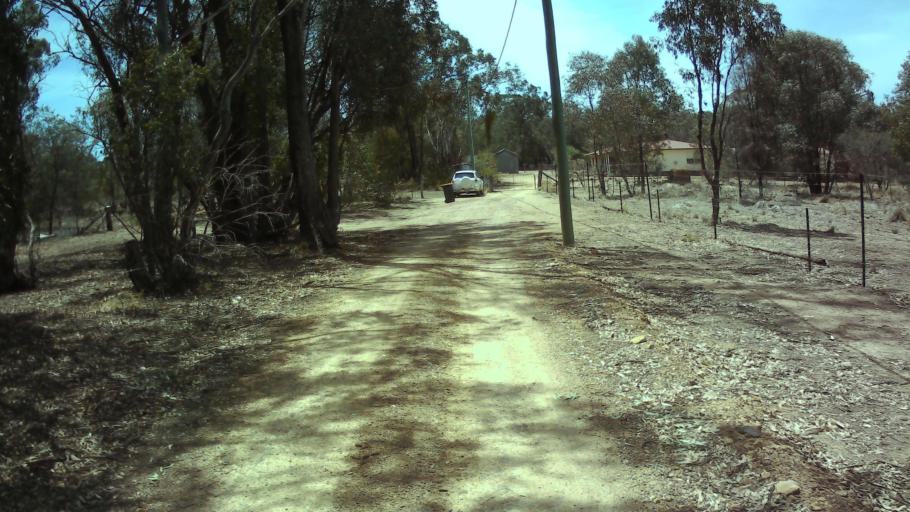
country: AU
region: New South Wales
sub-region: Weddin
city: Grenfell
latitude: -33.8867
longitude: 148.1697
